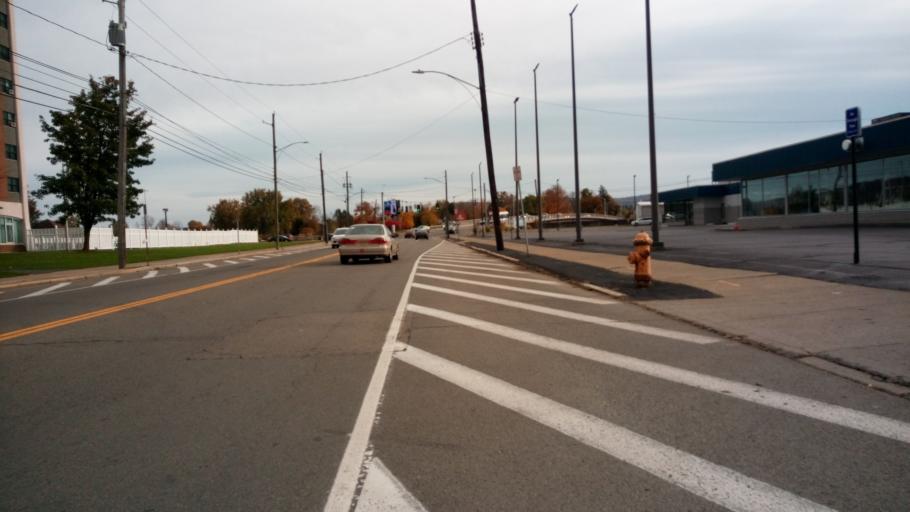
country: US
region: New York
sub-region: Chemung County
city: Elmira
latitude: 42.0898
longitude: -76.7984
